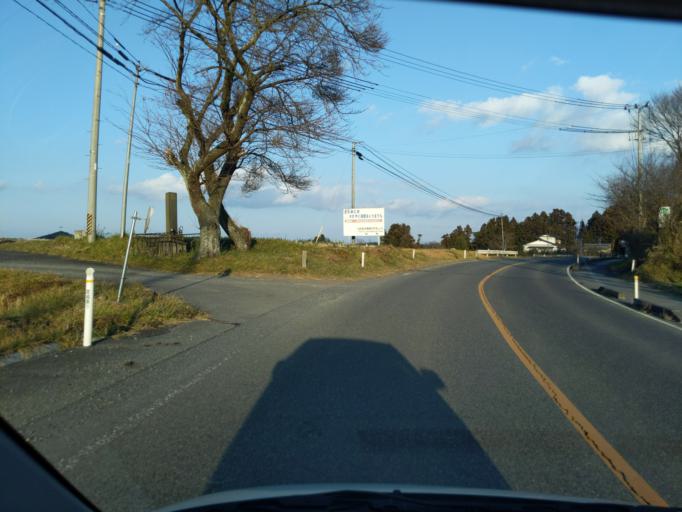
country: JP
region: Miyagi
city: Wakuya
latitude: 38.6774
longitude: 141.1140
